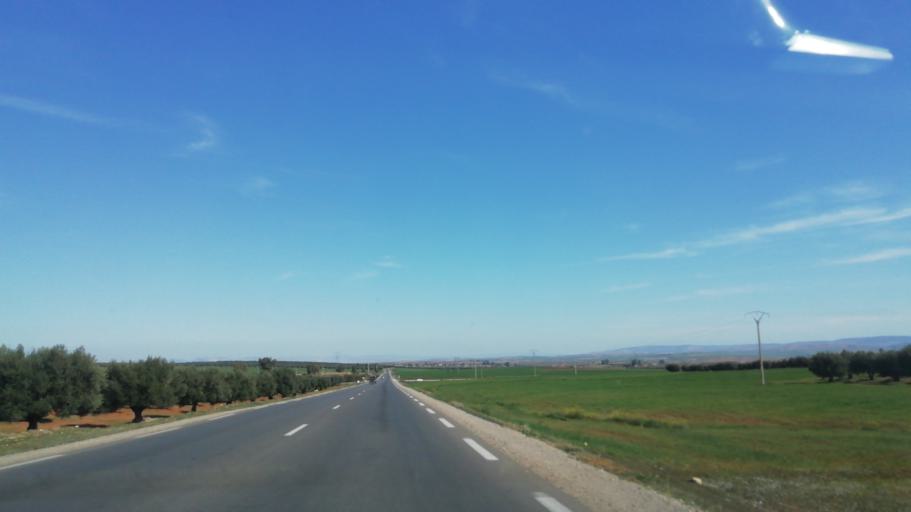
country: DZ
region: Mascara
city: Mascara
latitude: 35.4176
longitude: 0.4094
